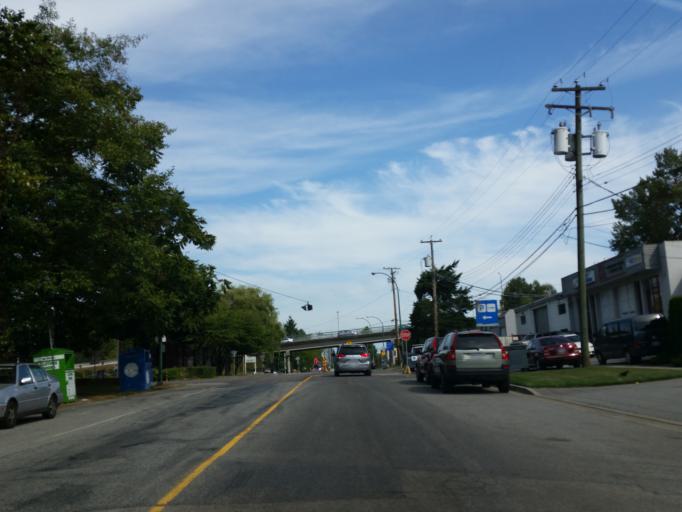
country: CA
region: British Columbia
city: Port Moody
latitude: 49.2789
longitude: -122.8522
